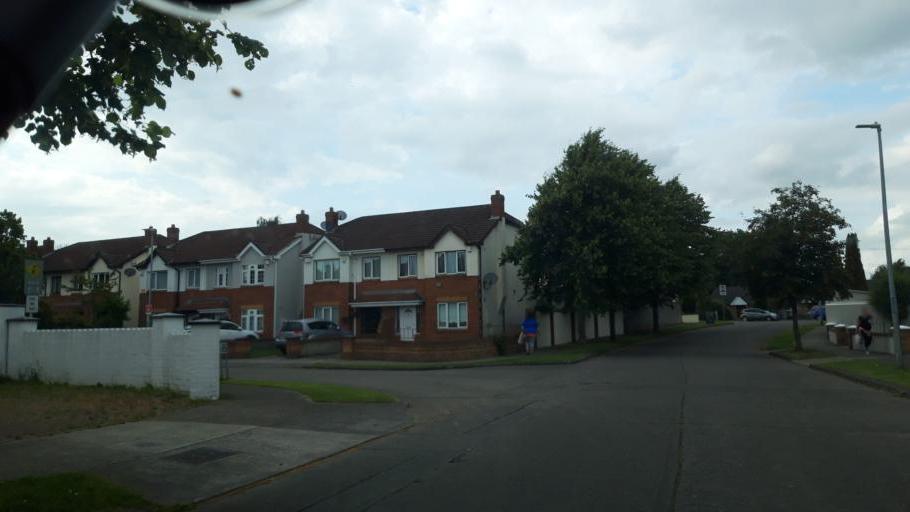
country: IE
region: Leinster
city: Hartstown
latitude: 53.3913
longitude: -6.4218
